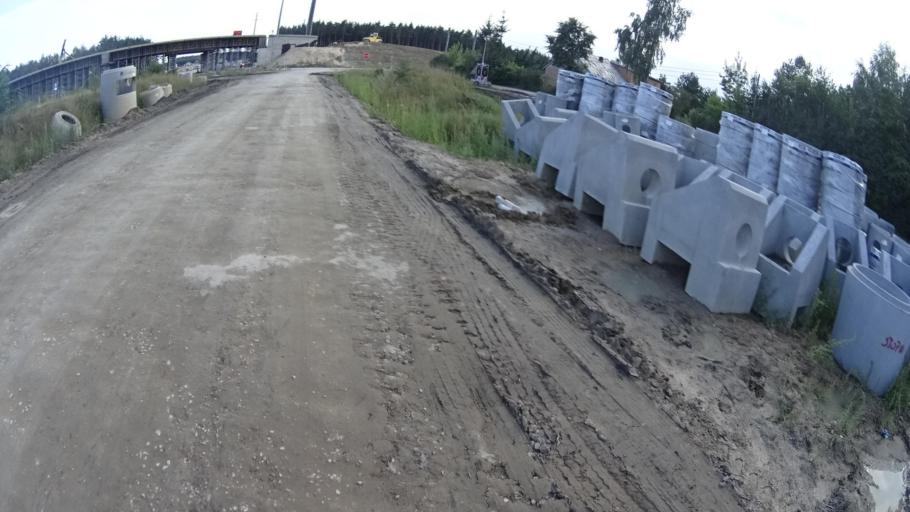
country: PL
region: Masovian Voivodeship
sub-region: Powiat piaseczynski
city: Tarczyn
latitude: 51.9796
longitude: 20.8645
